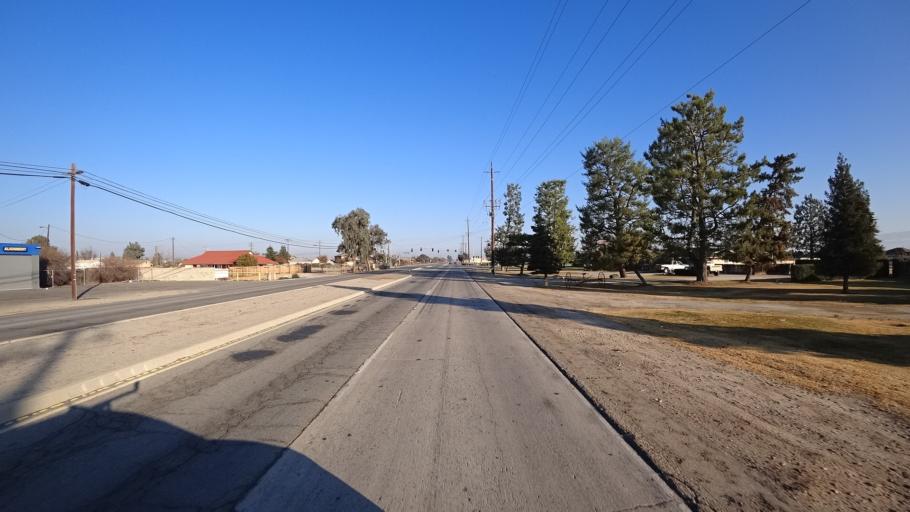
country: US
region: California
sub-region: Kern County
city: Greenfield
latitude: 35.2871
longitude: -119.0031
